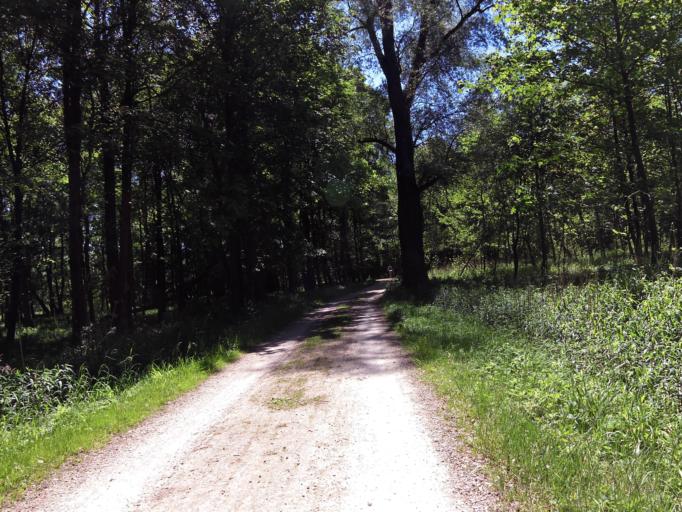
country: DE
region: Bavaria
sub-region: Upper Bavaria
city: Neufahrn bei Freising
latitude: 48.3043
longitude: 11.6999
